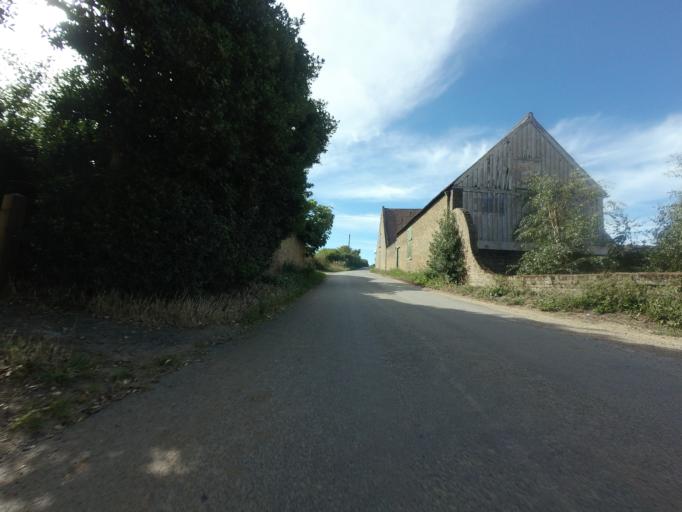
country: GB
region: England
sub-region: Kent
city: Herne Bay
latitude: 51.3687
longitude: 1.1881
